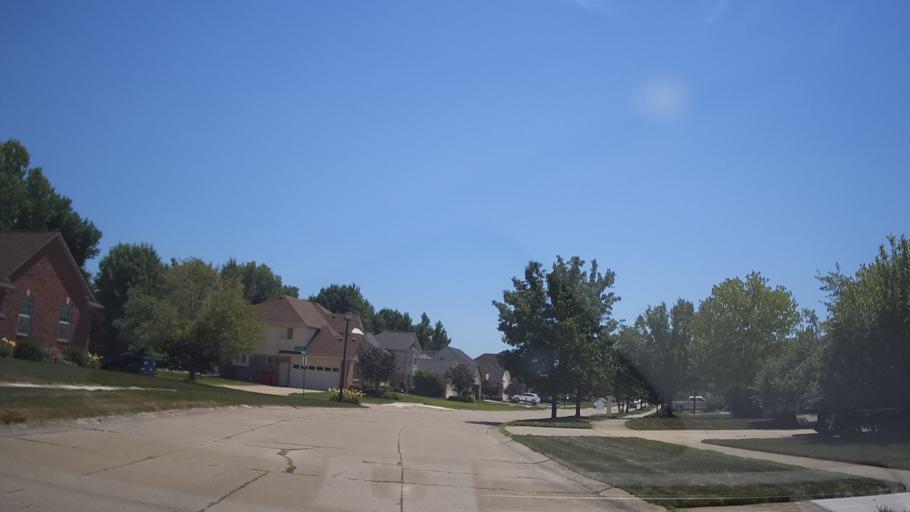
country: US
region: Michigan
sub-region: Macomb County
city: Mount Clemens
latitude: 42.6573
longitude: -82.9129
